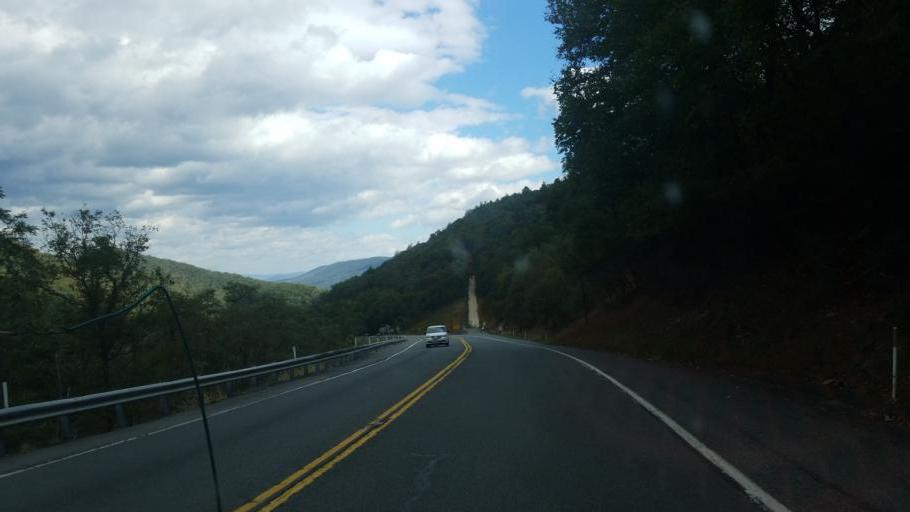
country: US
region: Pennsylvania
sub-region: Fulton County
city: McConnellsburg
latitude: 39.9294
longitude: -77.9344
